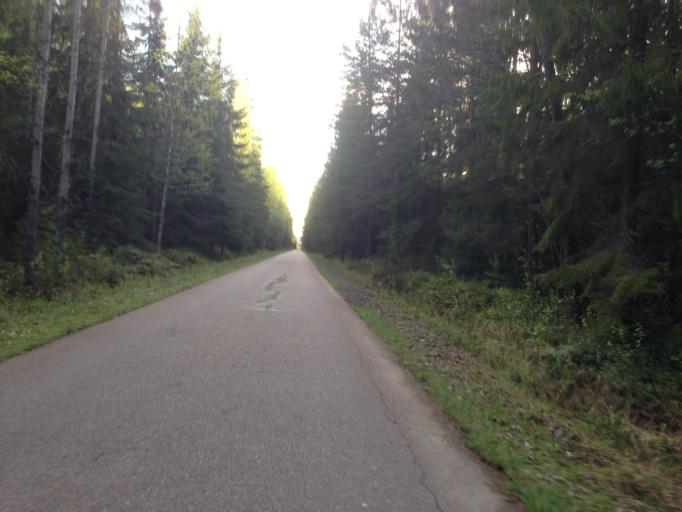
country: SE
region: Dalarna
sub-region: Ludvika Kommun
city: Ludvika
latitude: 60.1394
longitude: 15.1247
